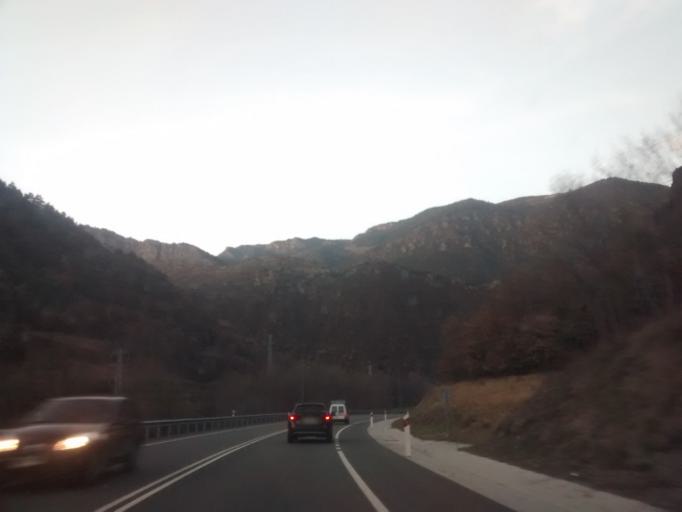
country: AD
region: Sant Julia de Loria
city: Sant Julia de Loria
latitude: 42.4206
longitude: 1.4628
